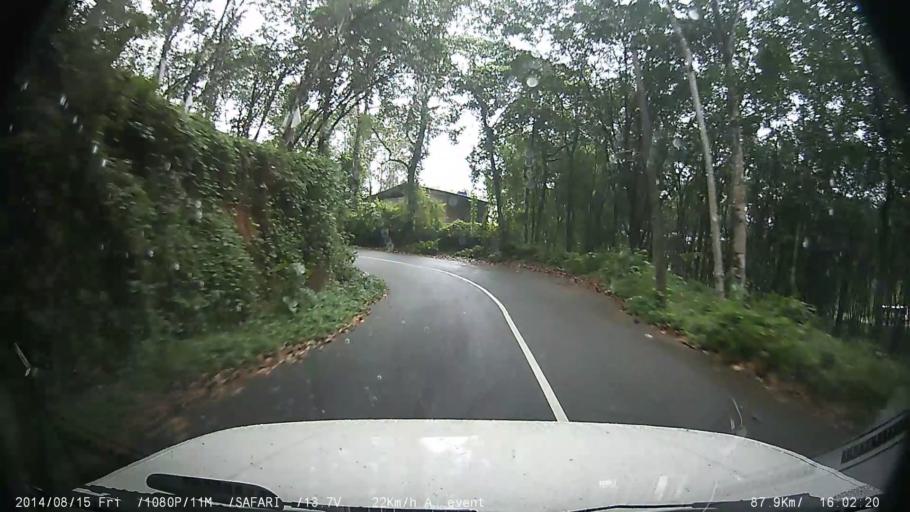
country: IN
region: Kerala
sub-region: Kottayam
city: Lalam
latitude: 9.7695
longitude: 76.7098
